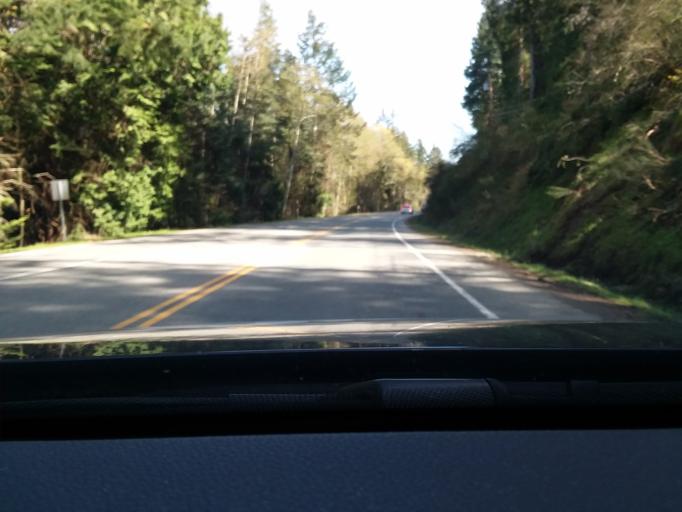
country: CA
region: British Columbia
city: North Saanich
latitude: 48.8517
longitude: -123.4560
